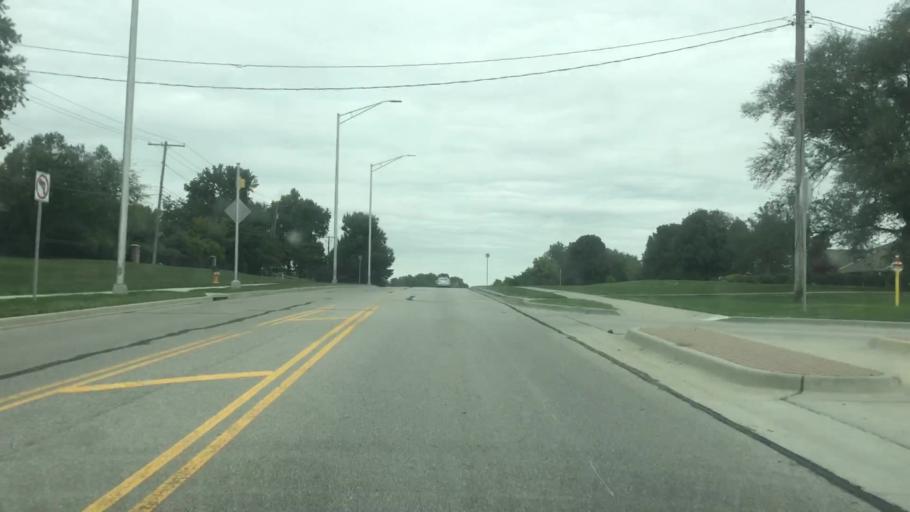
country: US
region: Kansas
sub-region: Johnson County
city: Lenexa
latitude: 38.9781
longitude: -94.7797
